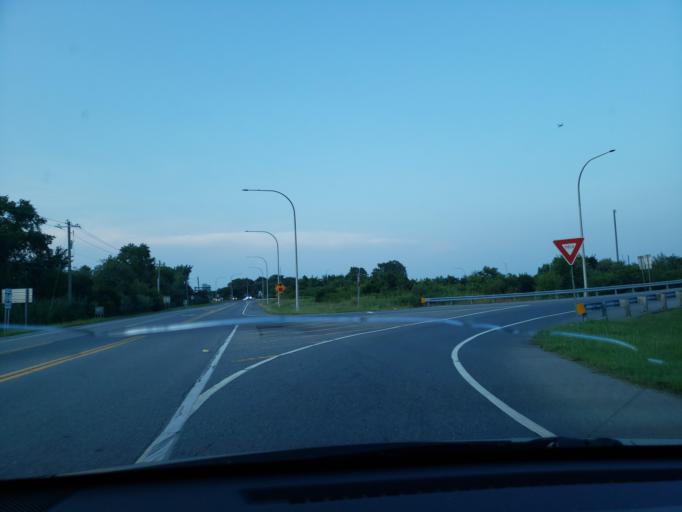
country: US
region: Delaware
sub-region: Kent County
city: Riverview
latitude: 39.0141
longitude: -75.4632
